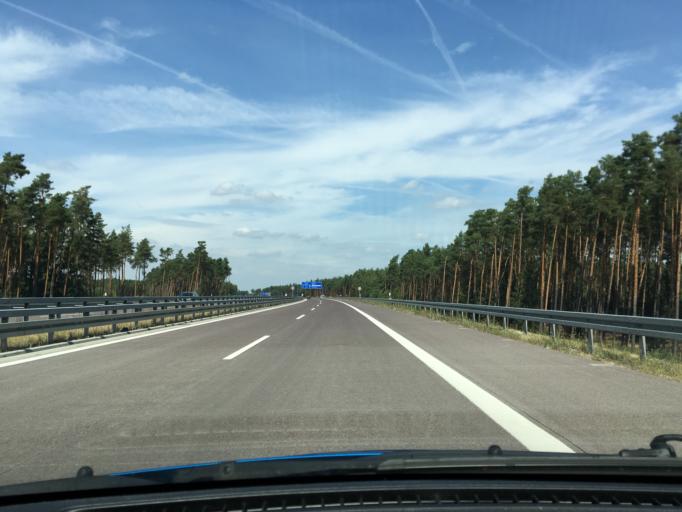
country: DE
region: Mecklenburg-Vorpommern
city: Gross Laasch
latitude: 53.4049
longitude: 11.5314
